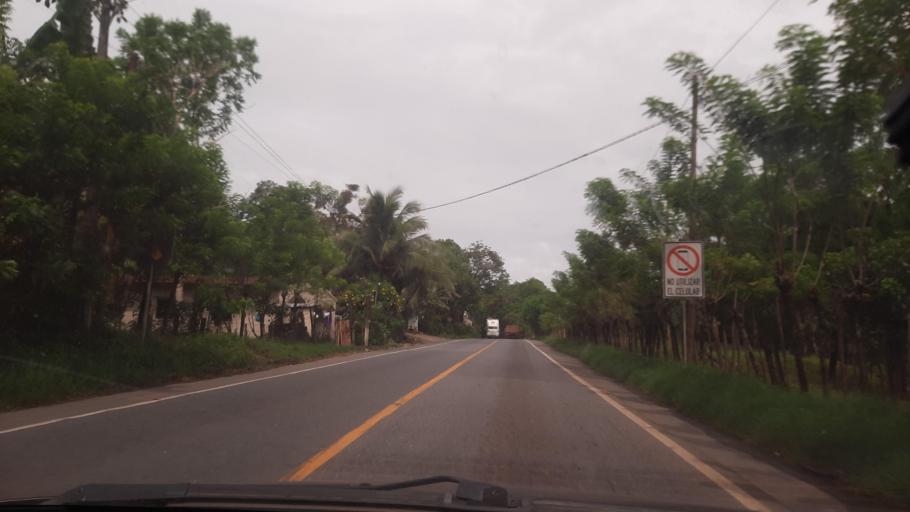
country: GT
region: Izabal
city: Morales
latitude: 15.5233
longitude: -88.7865
